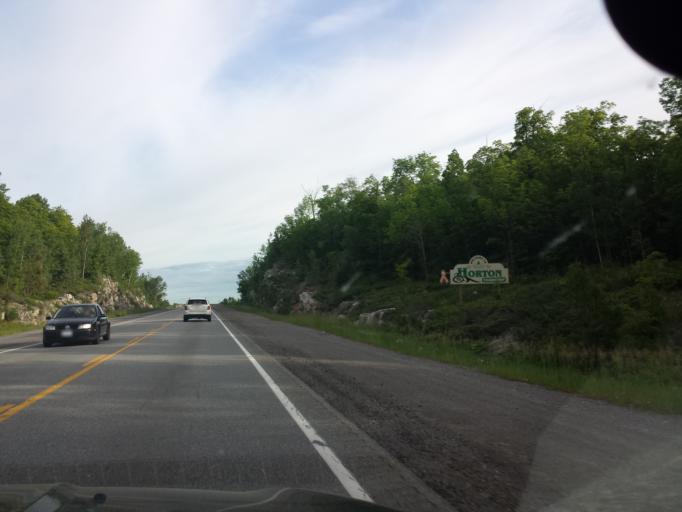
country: CA
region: Ontario
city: Renfrew
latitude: 45.4535
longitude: -76.6065
